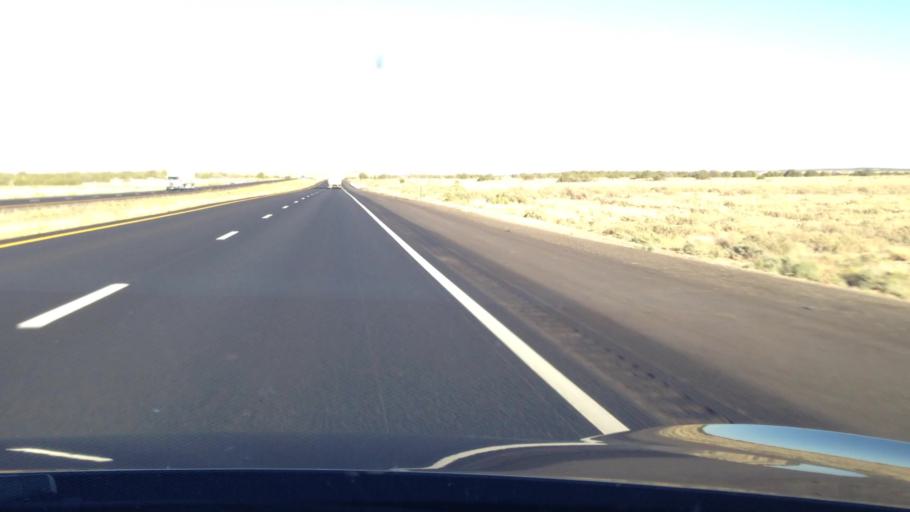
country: US
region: New Mexico
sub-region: Cibola County
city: Laguna
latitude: 35.0269
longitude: -107.4359
